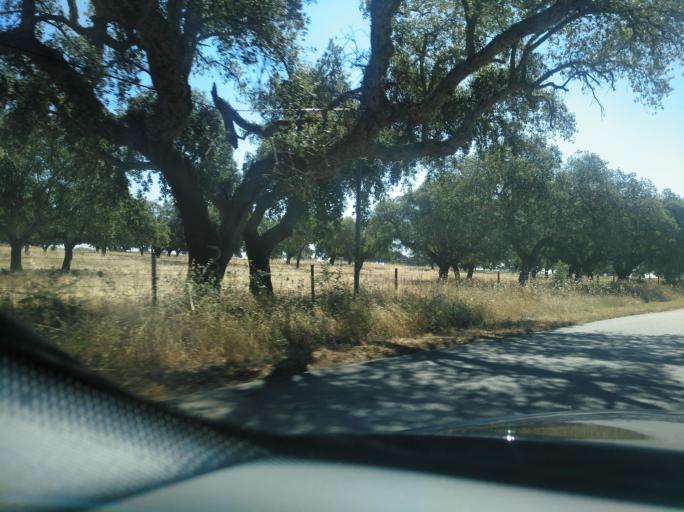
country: PT
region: Portalegre
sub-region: Arronches
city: Arronches
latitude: 38.9940
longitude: -7.3446
